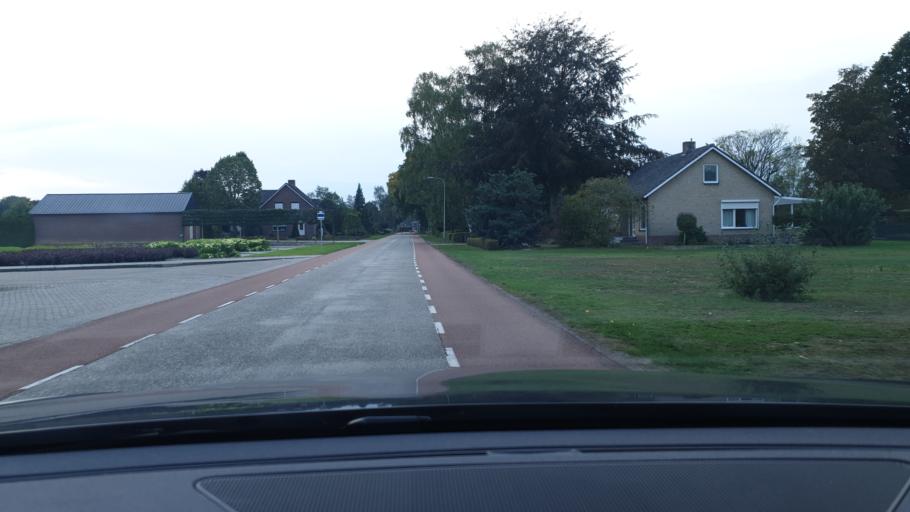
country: NL
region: Limburg
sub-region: Gemeente Venlo
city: Arcen
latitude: 51.4597
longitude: 6.1471
